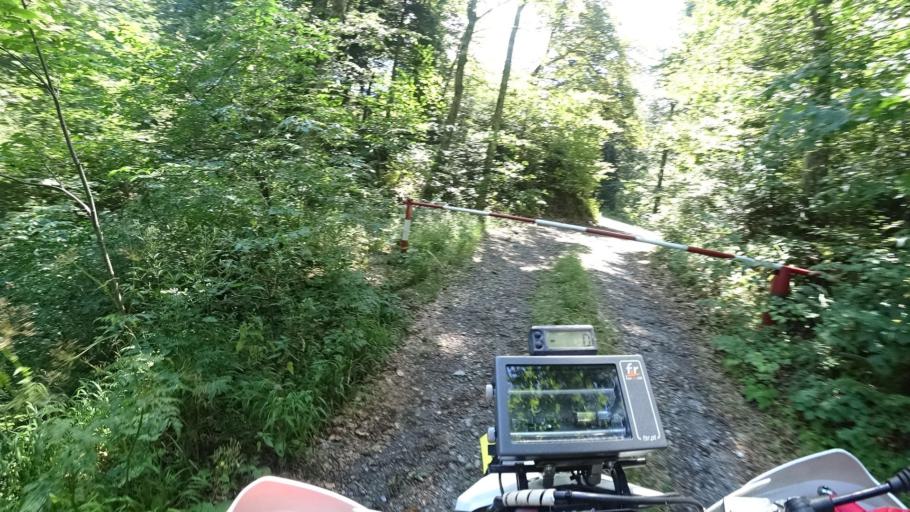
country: HR
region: Primorsko-Goranska
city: Vrbovsko
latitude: 45.2789
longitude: 15.1062
